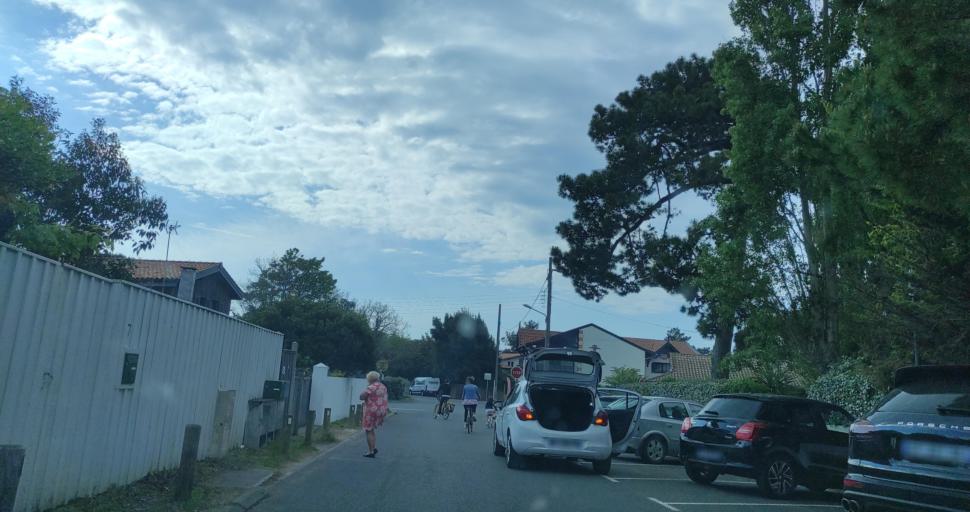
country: FR
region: Aquitaine
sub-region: Departement de la Gironde
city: Arcachon
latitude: 44.6557
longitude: -1.2409
